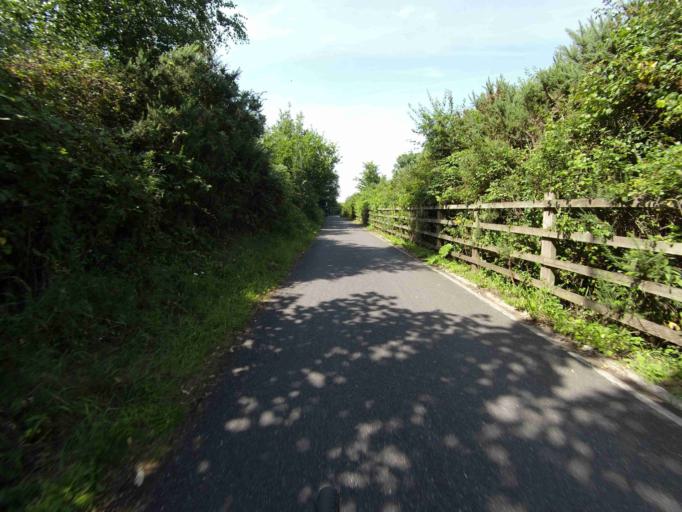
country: GB
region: England
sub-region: Devon
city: Topsham
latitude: 50.6784
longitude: -3.4508
